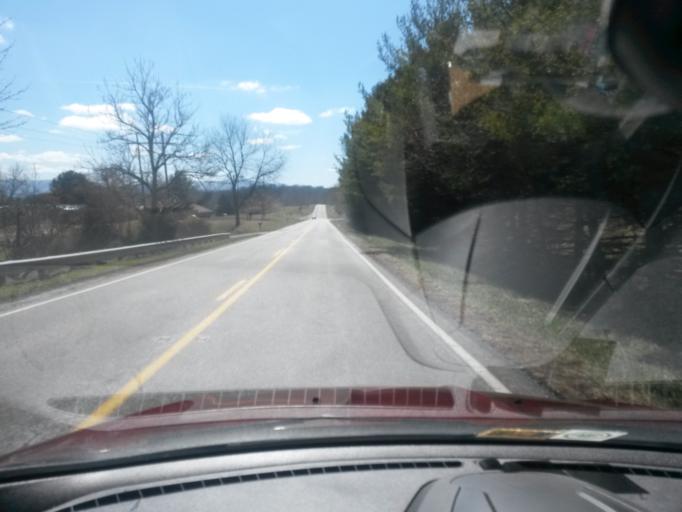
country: US
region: Virginia
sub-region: Augusta County
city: Stuarts Draft
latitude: 38.0464
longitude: -79.0538
